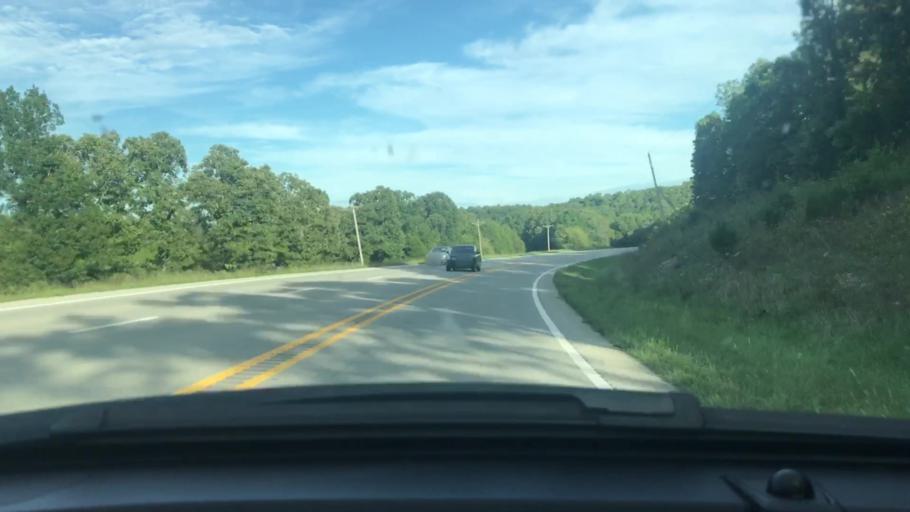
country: US
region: Arkansas
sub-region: Sharp County
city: Cherokee Village
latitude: 36.2748
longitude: -91.3591
